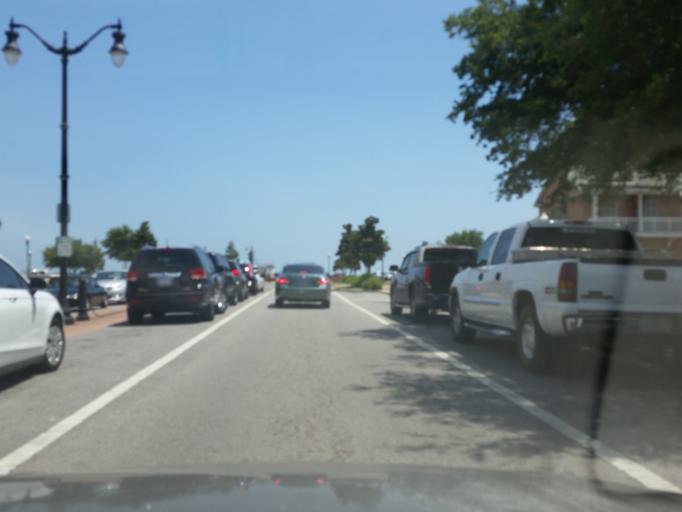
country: US
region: Florida
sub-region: Escambia County
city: Pensacola
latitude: 30.4033
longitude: -87.2133
